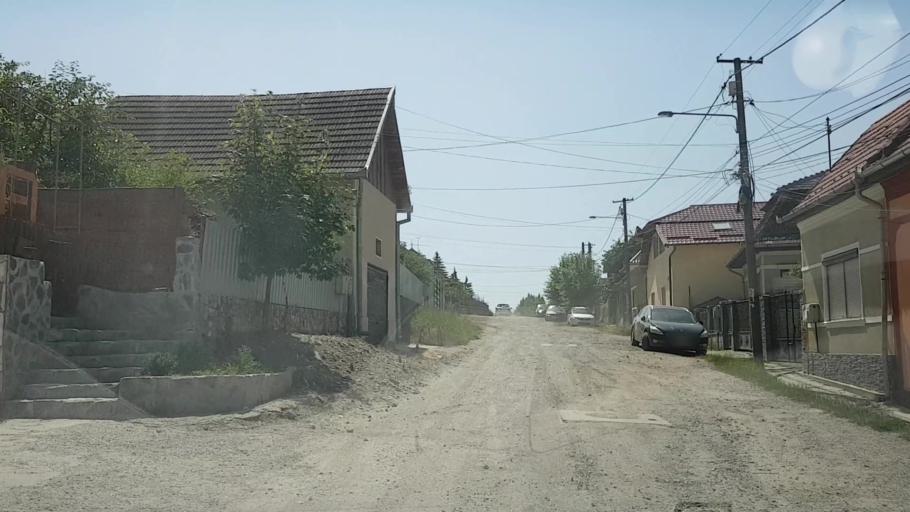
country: RO
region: Cluj
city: Turda
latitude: 46.5788
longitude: 23.7830
